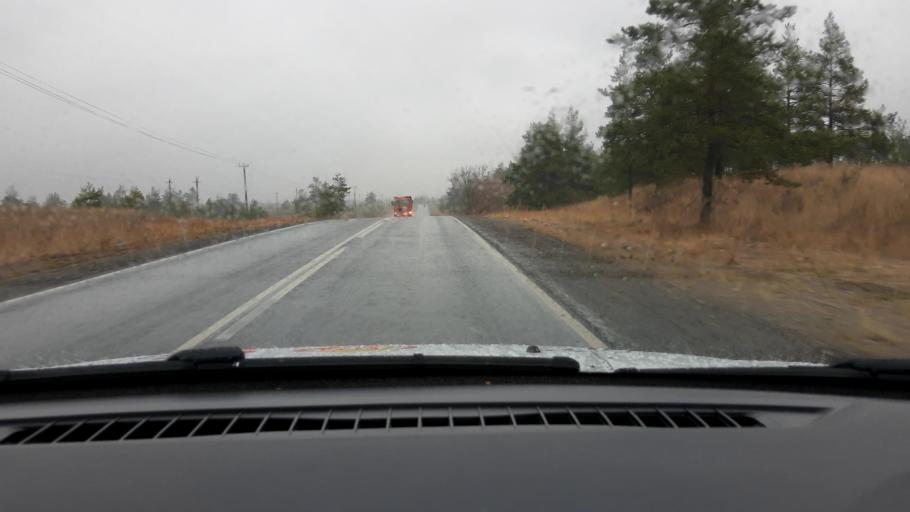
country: RU
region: Nizjnij Novgorod
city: Babino
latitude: 56.2694
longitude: 43.5927
